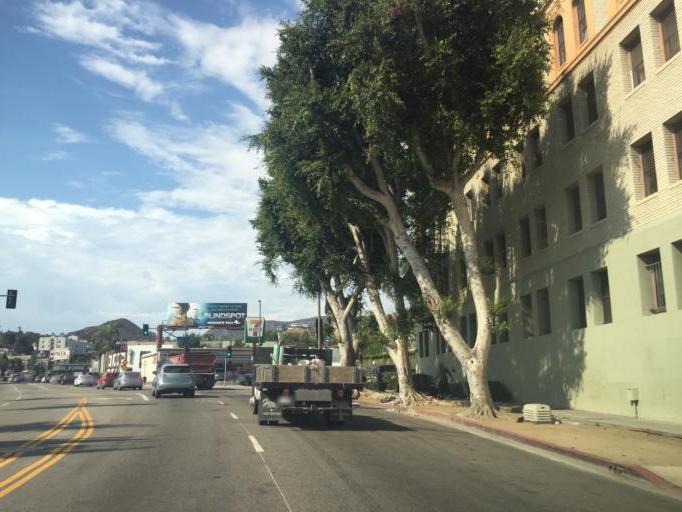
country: US
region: California
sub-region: Los Angeles County
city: Hollywood
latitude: 34.1035
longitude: -118.3296
